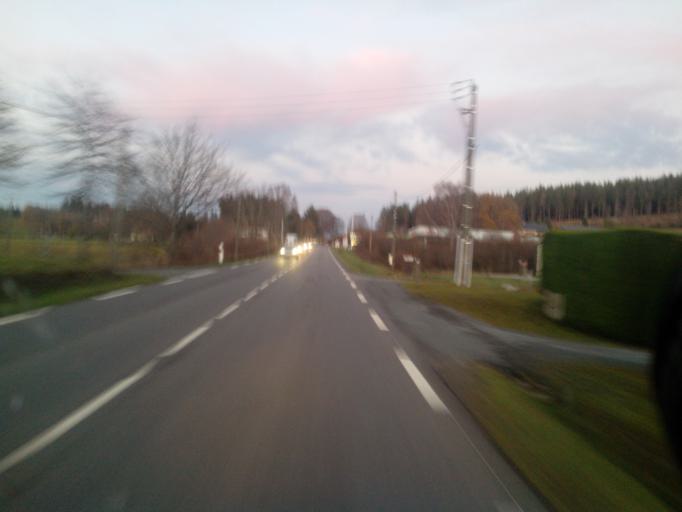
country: FR
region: Limousin
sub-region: Departement de la Correze
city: Ussel
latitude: 45.5075
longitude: 2.2443
